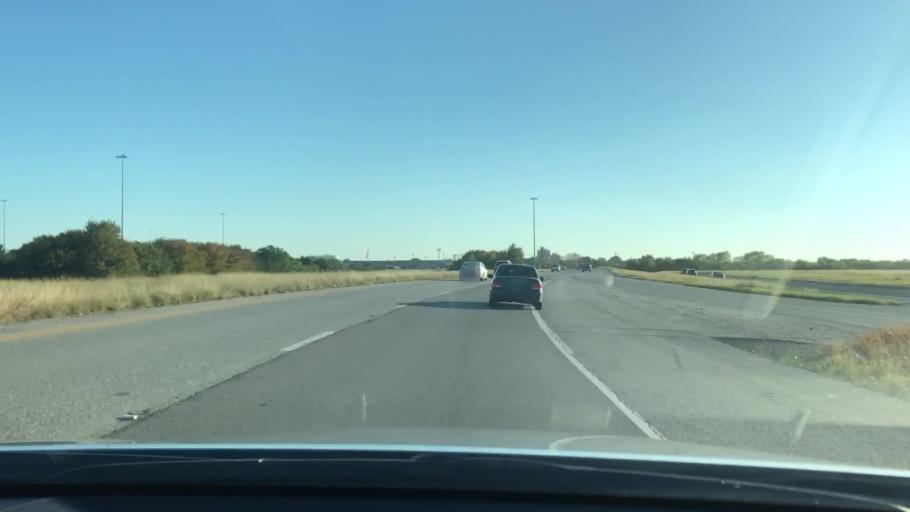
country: US
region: Texas
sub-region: Bexar County
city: Kirby
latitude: 29.4551
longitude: -98.4045
